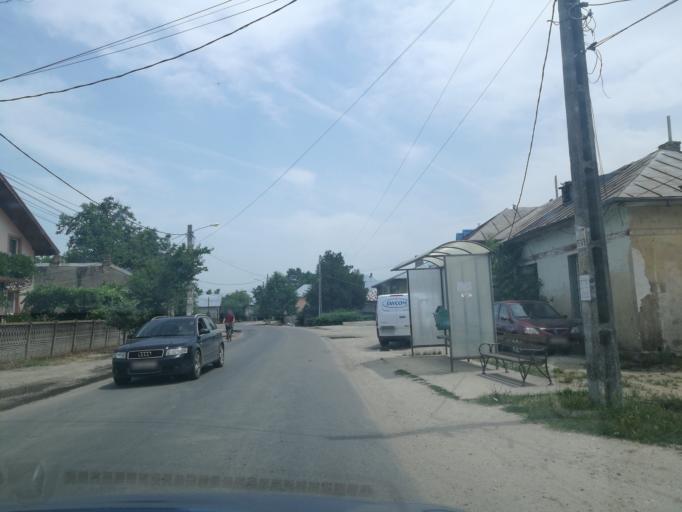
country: RO
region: Ilfov
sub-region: Comuna Vidra
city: Vidra
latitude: 44.2645
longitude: 26.1531
